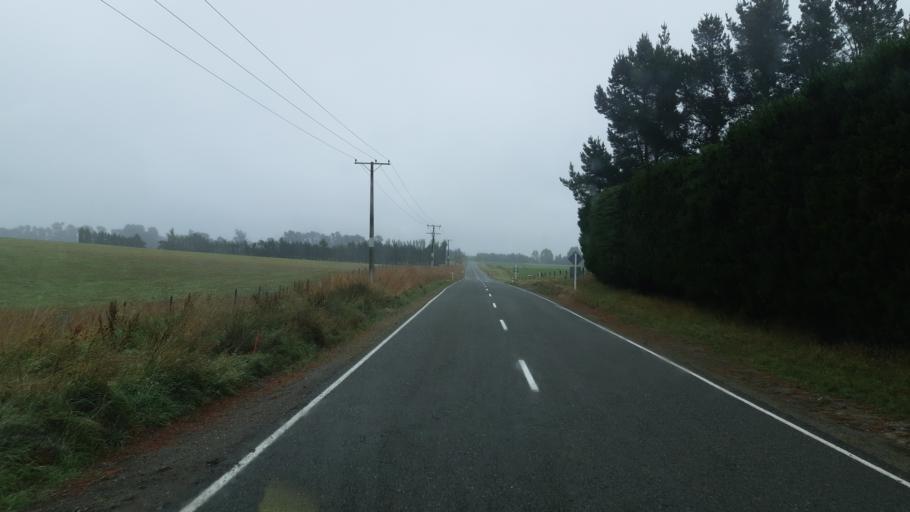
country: NZ
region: Otago
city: Oamaru
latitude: -44.9278
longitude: 170.8015
